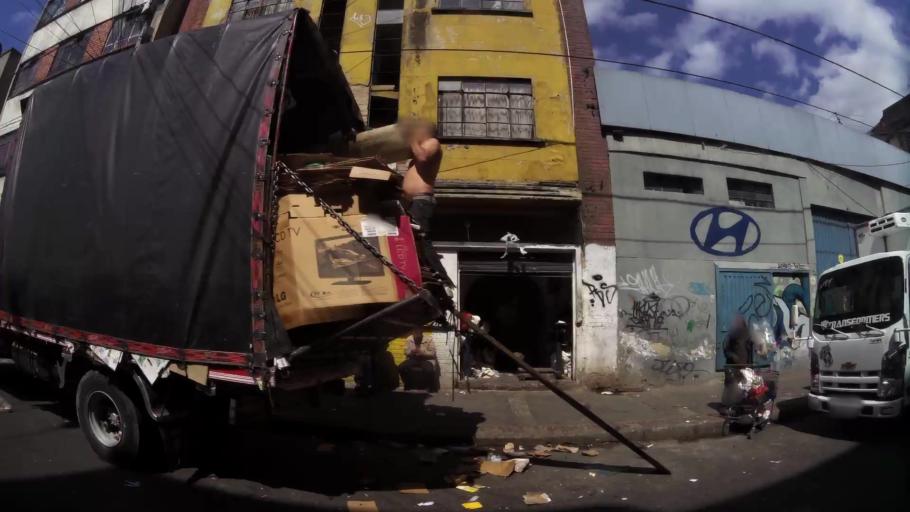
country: CO
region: Bogota D.C.
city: Bogota
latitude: 4.6137
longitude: -74.0782
